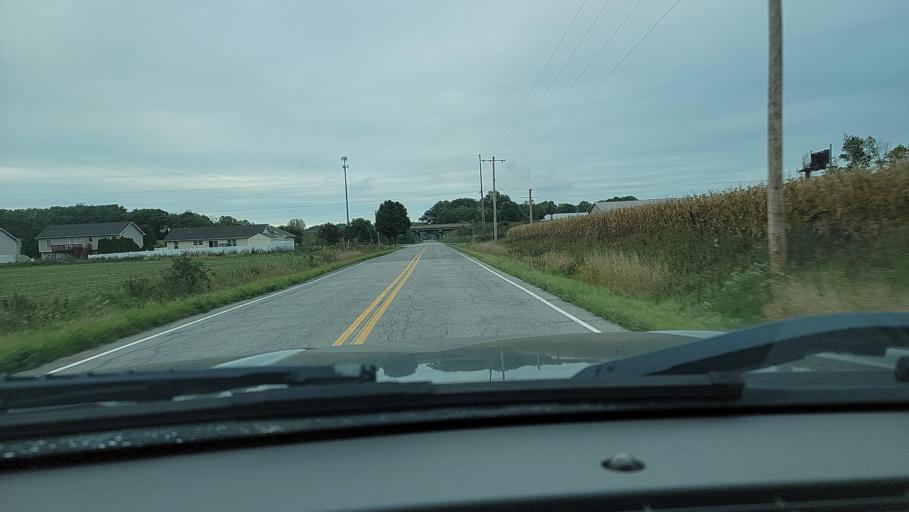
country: US
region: Indiana
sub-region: Porter County
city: Portage
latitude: 41.5710
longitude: -87.1534
